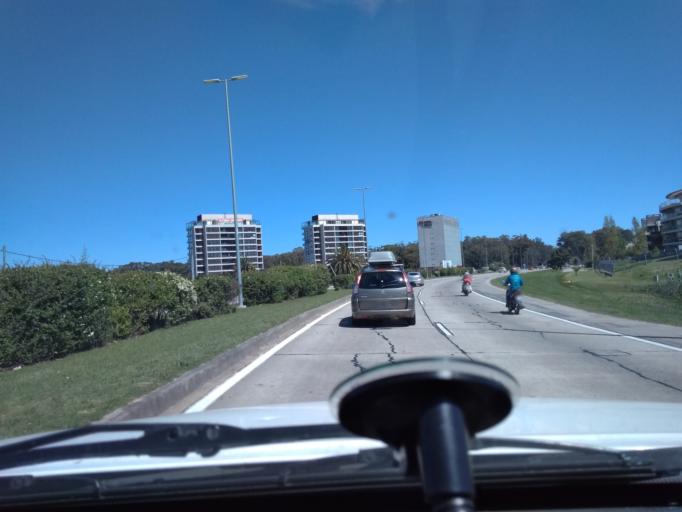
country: UY
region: Canelones
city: Barra de Carrasco
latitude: -34.8480
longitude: -56.0237
